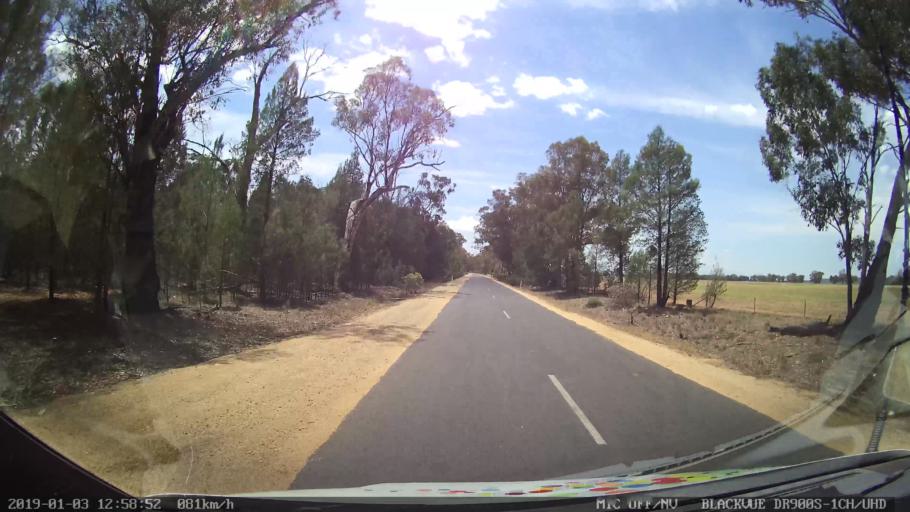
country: AU
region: New South Wales
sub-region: Cabonne
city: Canowindra
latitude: -33.6400
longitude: 148.3813
